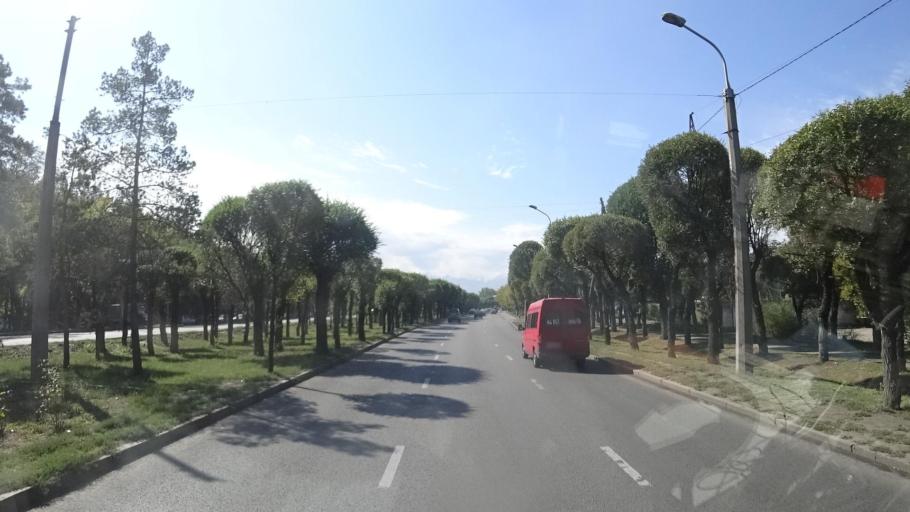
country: KZ
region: Almaty Oblysy
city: Pervomayskiy
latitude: 43.3357
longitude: 76.9811
